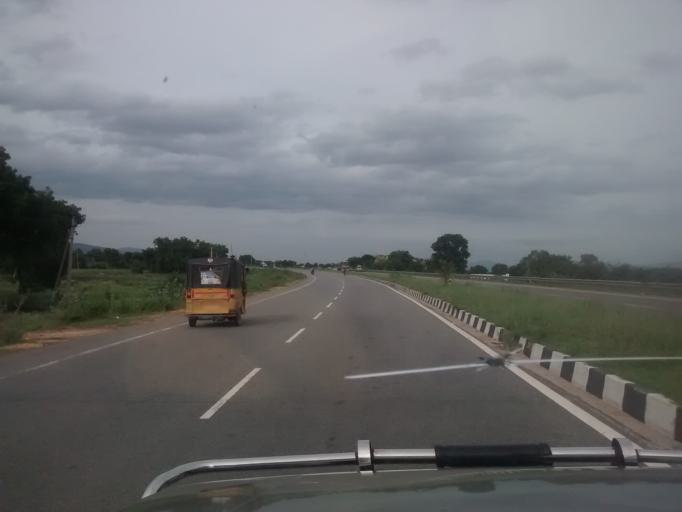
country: IN
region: Andhra Pradesh
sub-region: Chittoor
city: Narasingapuram
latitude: 13.5985
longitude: 79.3568
